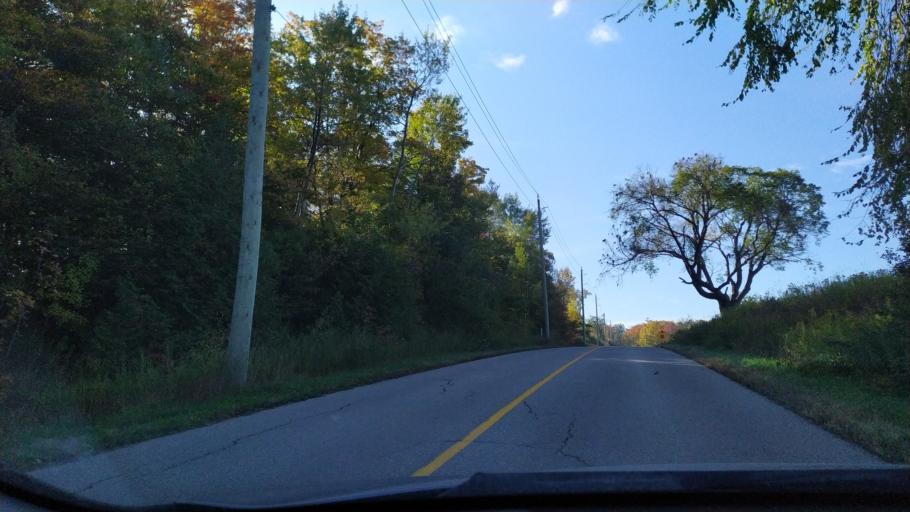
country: CA
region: Ontario
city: Waterloo
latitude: 43.4897
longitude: -80.6576
